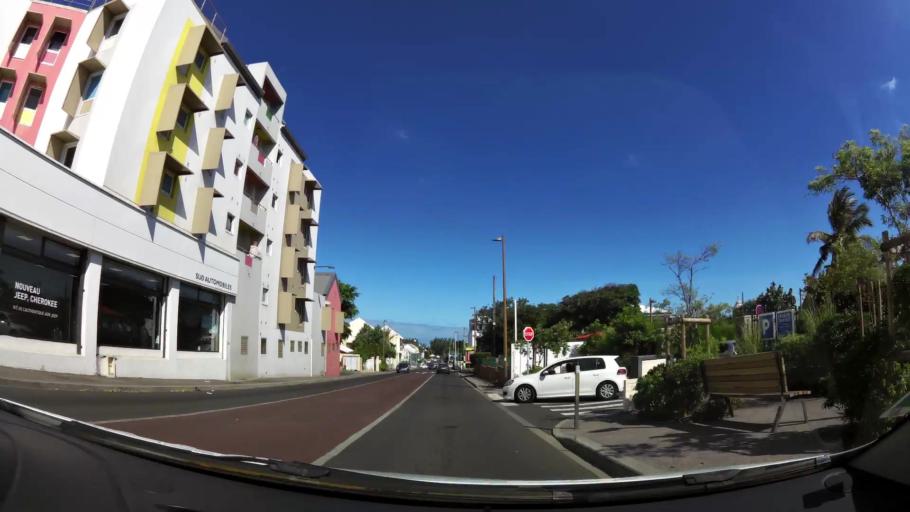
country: RE
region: Reunion
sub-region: Reunion
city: Saint-Pierre
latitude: -21.3348
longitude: 55.4599
